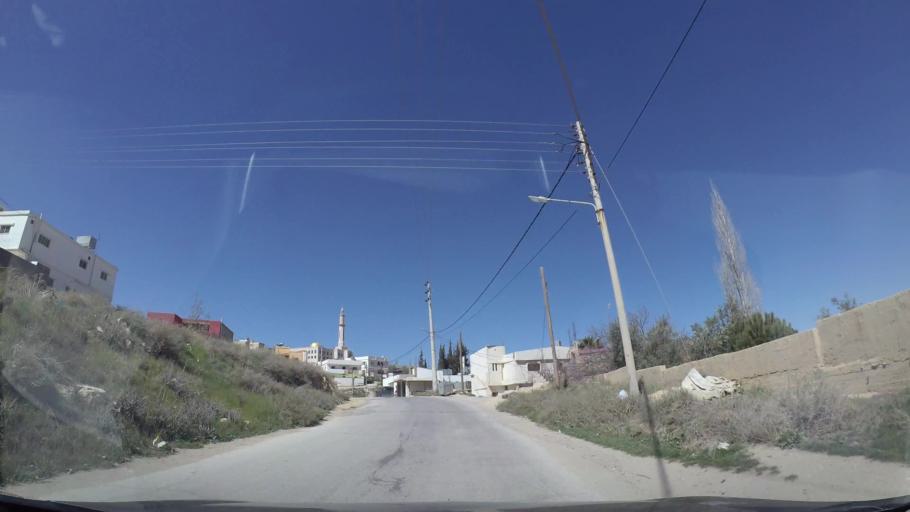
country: JO
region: Tafielah
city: At Tafilah
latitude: 30.8190
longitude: 35.5850
